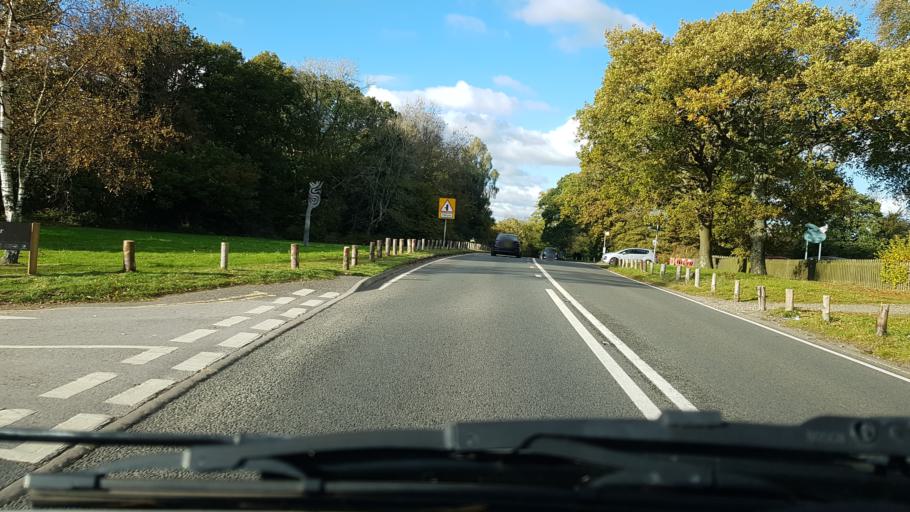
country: GB
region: England
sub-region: Surrey
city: Chilworth
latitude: 51.2328
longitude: -0.5056
